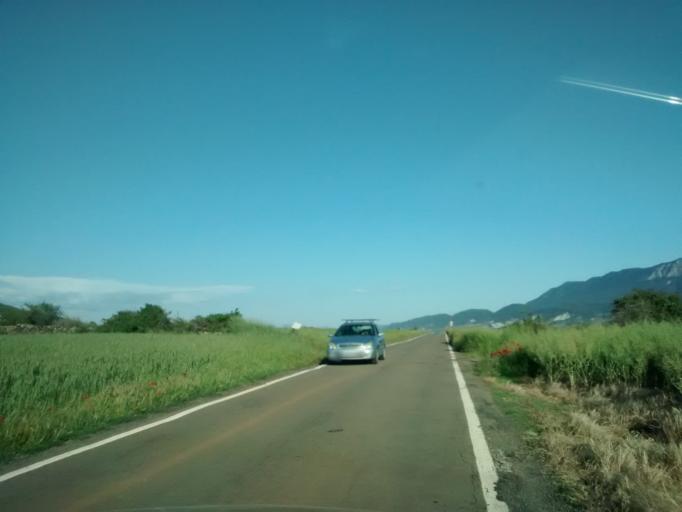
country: ES
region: Aragon
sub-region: Provincia de Huesca
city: Jaca
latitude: 42.5882
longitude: -0.6071
